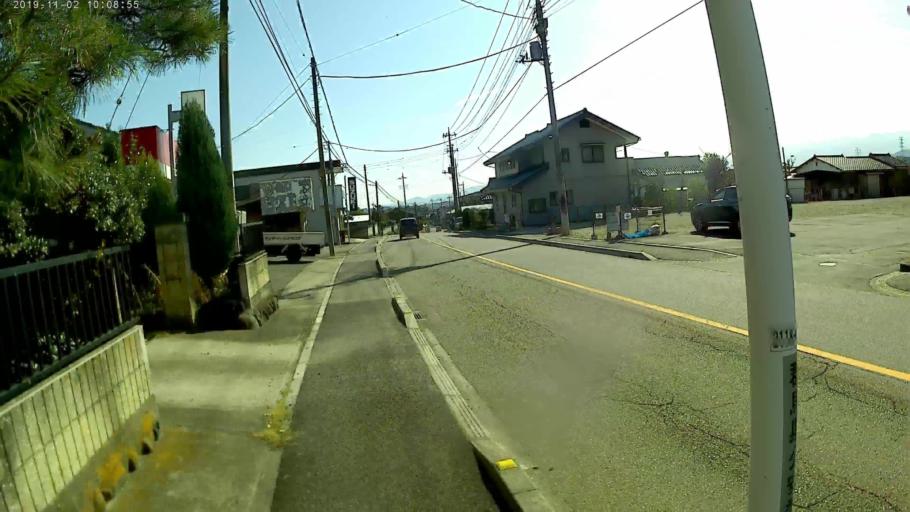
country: JP
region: Gunma
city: Annaka
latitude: 36.3181
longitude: 138.7891
